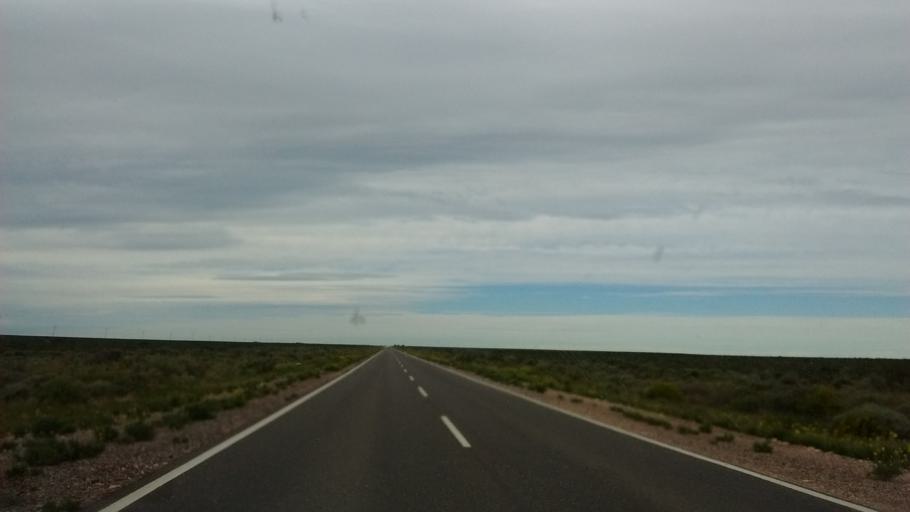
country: AR
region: Rio Negro
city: Contraalmirante Cordero
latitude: -38.3508
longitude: -68.0144
